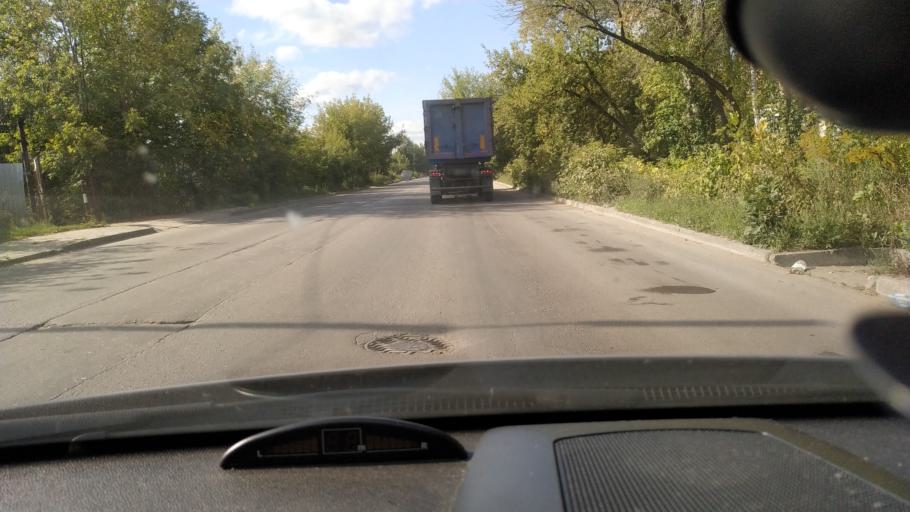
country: RU
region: Rjazan
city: Ryazan'
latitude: 54.6598
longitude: 39.6328
